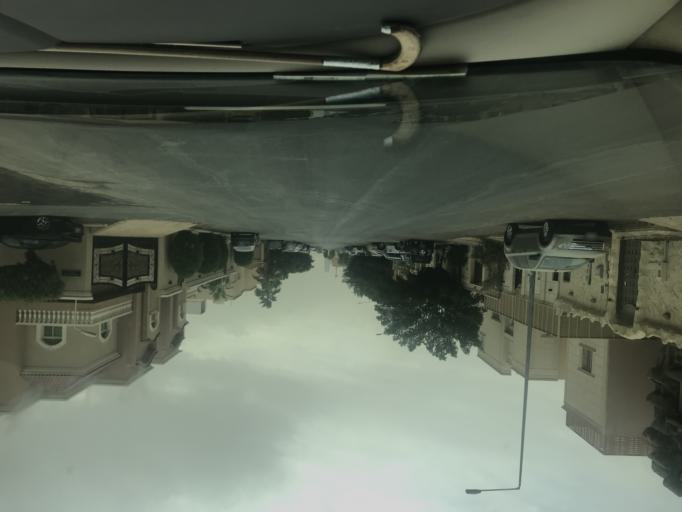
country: SA
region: Ar Riyad
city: Riyadh
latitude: 24.7873
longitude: 46.6976
